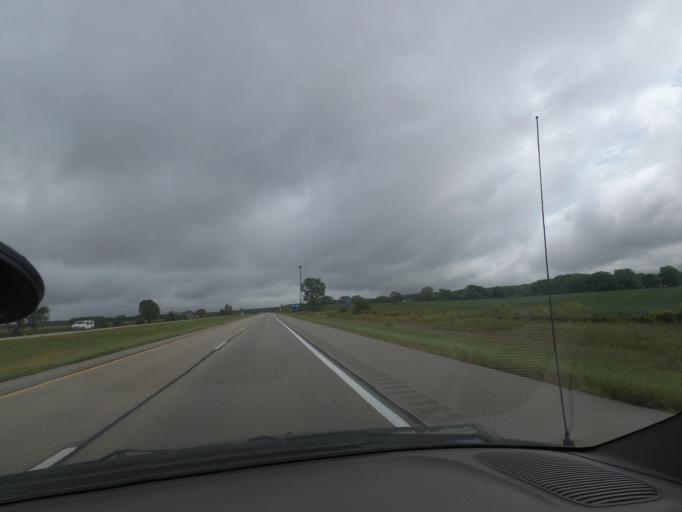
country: US
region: Illinois
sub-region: Piatt County
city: Monticello
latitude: 40.0402
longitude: -88.5891
